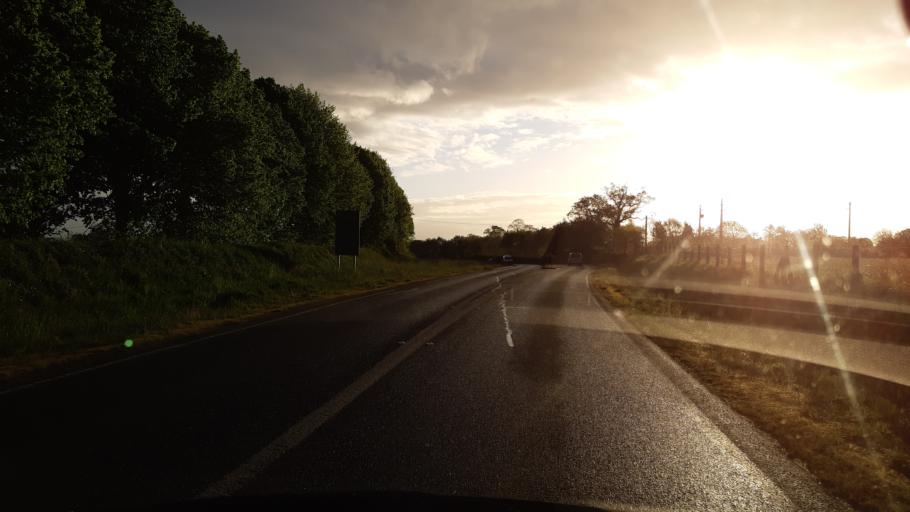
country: FR
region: Lower Normandy
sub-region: Departement de la Manche
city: Agneaux
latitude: 49.0306
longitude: -1.1386
